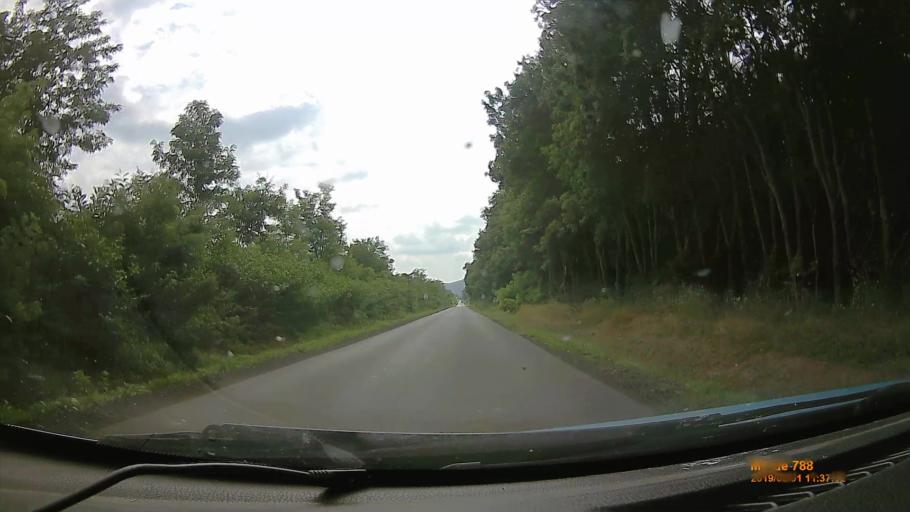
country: HU
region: Baranya
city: Villany
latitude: 45.9109
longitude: 18.3800
